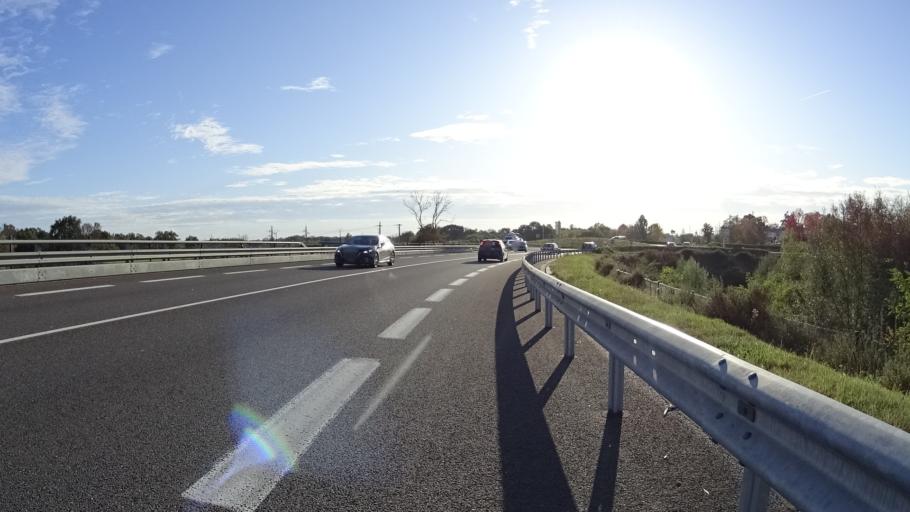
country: FR
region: Aquitaine
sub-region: Departement des Landes
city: Saint-Paul-les-Dax
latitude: 43.7251
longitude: -1.0358
